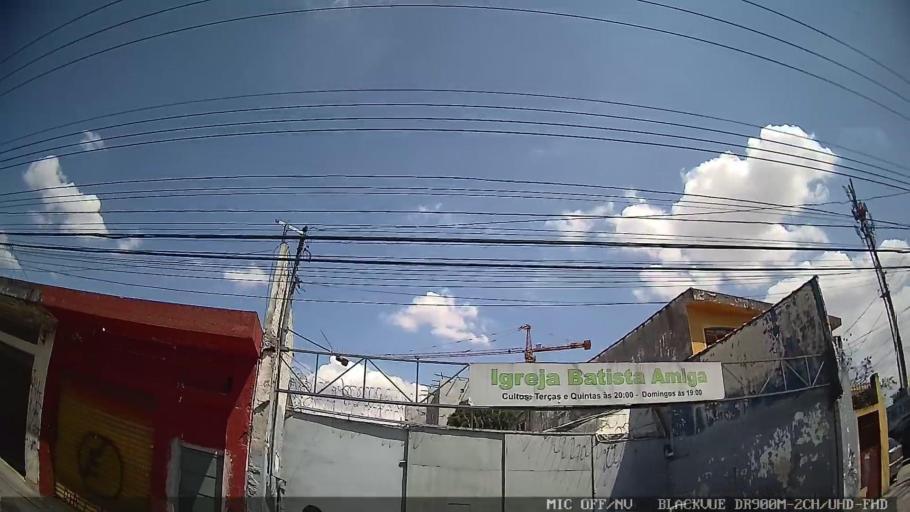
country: BR
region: Sao Paulo
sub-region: Guarulhos
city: Guarulhos
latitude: -23.5053
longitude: -46.5209
